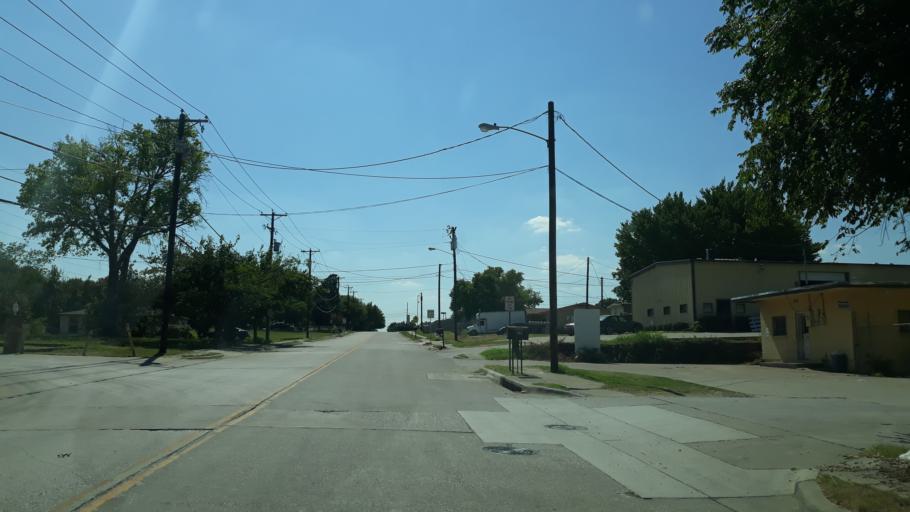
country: US
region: Texas
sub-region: Dallas County
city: Irving
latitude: 32.8172
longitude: -96.9971
